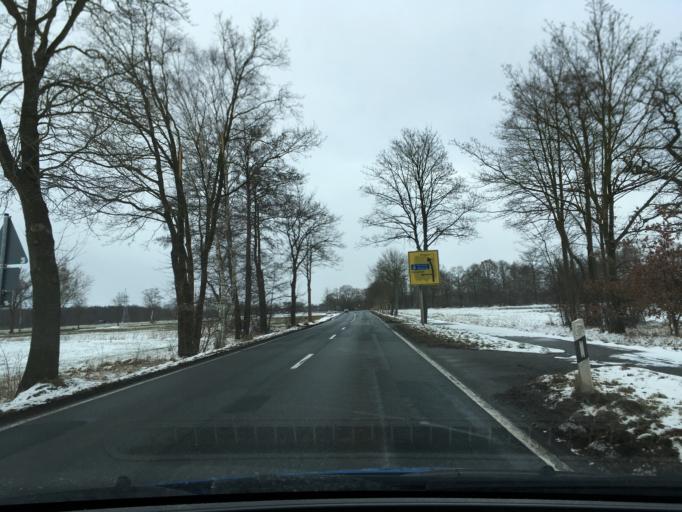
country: DE
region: Lower Saxony
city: Wulfsen
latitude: 53.3206
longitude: 10.1806
